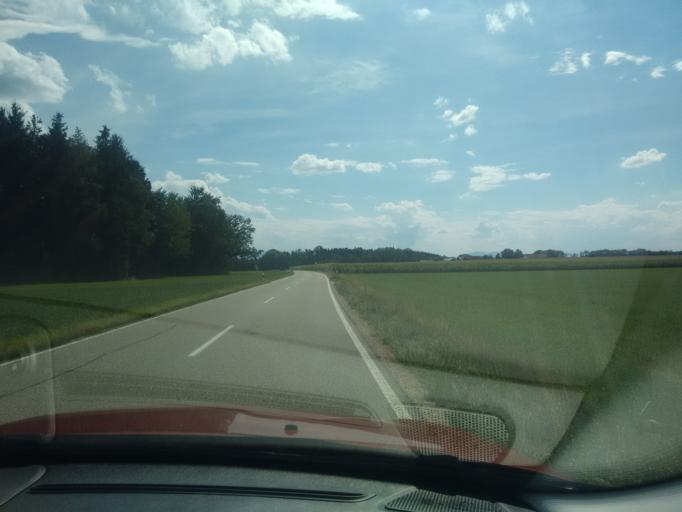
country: DE
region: Bavaria
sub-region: Upper Bavaria
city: Tacherting
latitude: 48.0589
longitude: 12.5944
